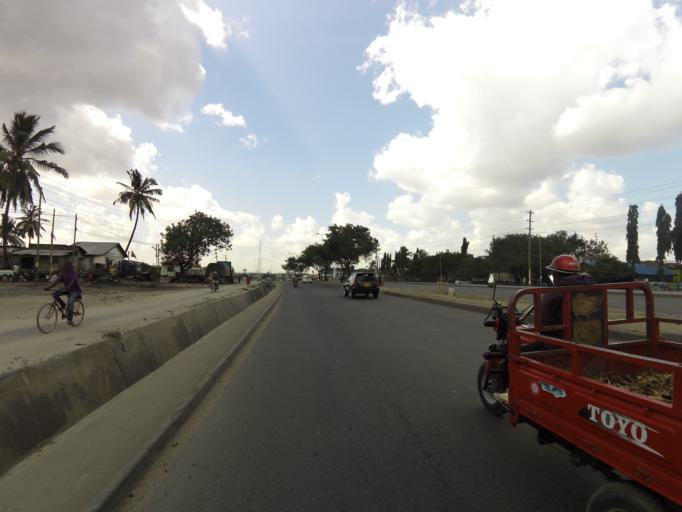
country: TZ
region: Dar es Salaam
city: Magomeni
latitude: -6.8129
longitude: 39.2175
